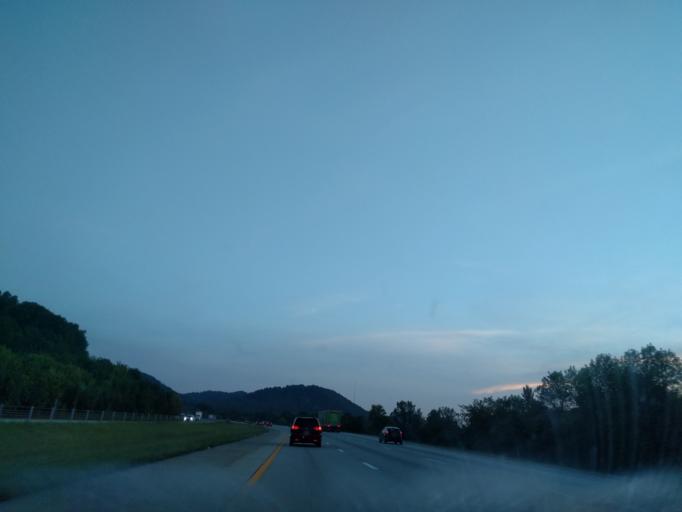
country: US
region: Kentucky
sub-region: Bullitt County
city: Lebanon Junction
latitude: 37.8997
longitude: -85.6976
